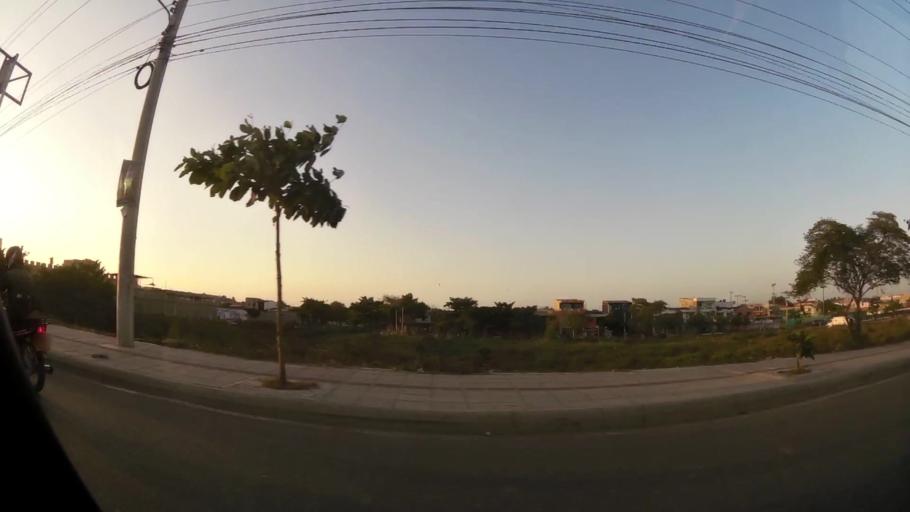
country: CO
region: Bolivar
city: Cartagena
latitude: 10.3980
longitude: -75.4722
